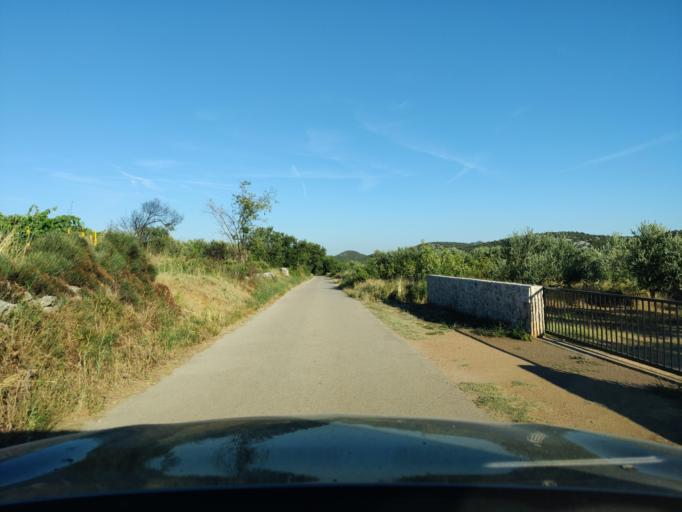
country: HR
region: Sibensko-Kniniska
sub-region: Grad Sibenik
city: Pirovac
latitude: 43.8643
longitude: 15.6984
